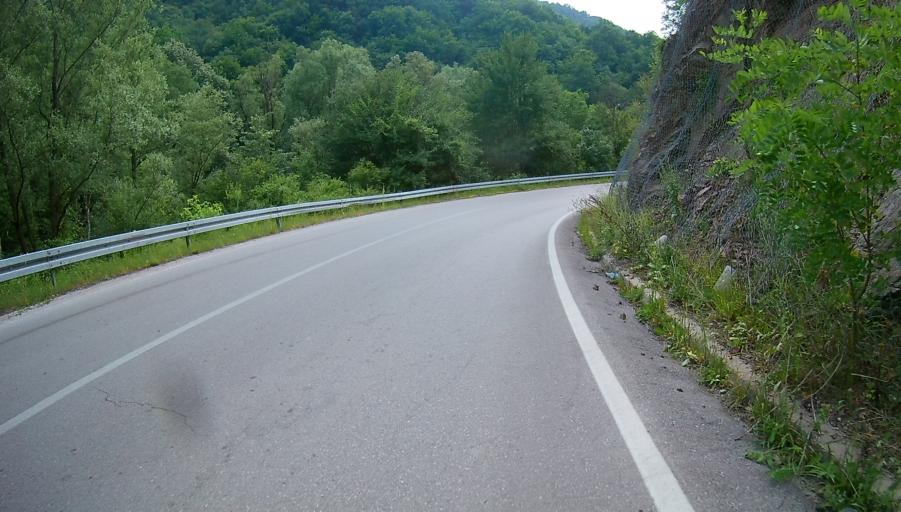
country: RS
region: Central Serbia
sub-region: Nisavski Okrug
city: Gadzin Han
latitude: 43.1810
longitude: 22.0350
